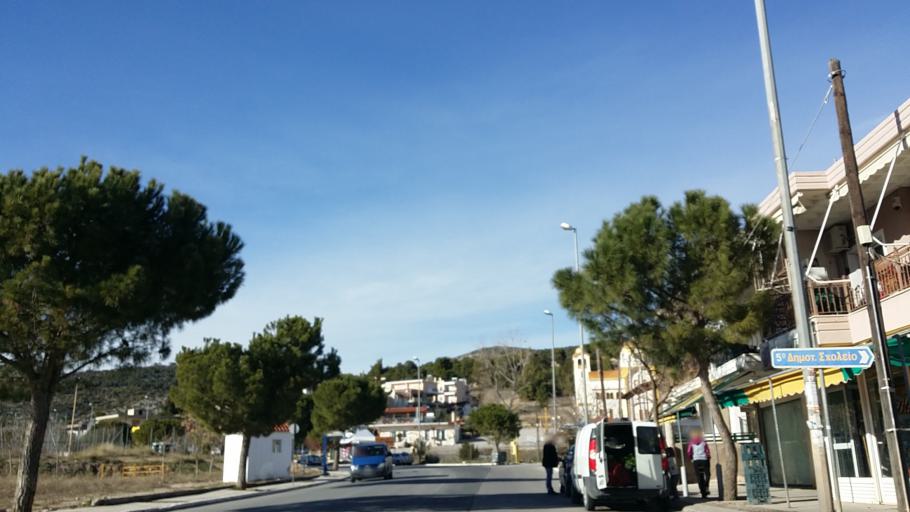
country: GR
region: Attica
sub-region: Nomarchia Dytikis Attikis
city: Ano Liosia
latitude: 38.0959
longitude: 23.6864
